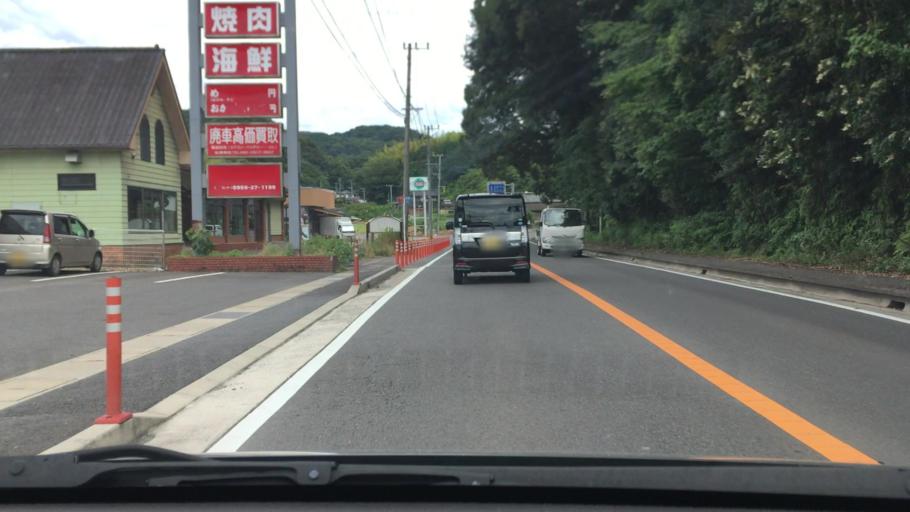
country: JP
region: Nagasaki
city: Togitsu
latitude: 32.9850
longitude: 129.7782
